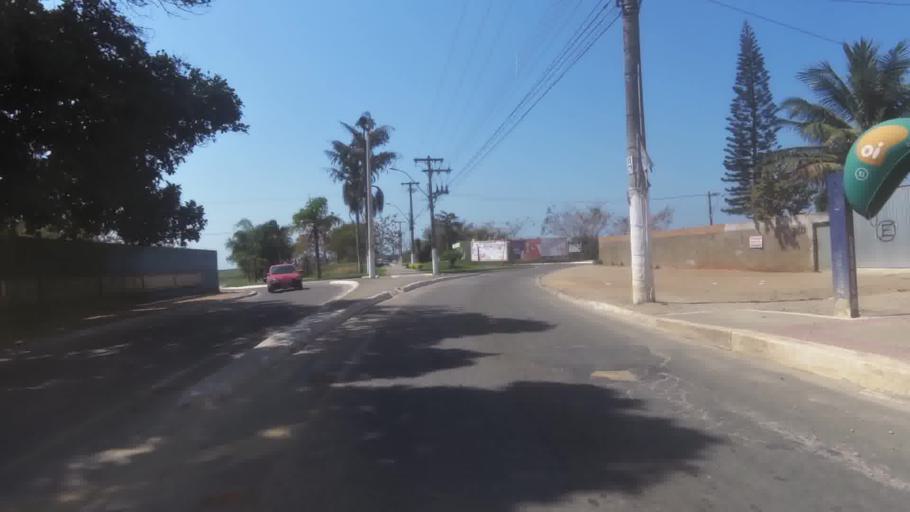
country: BR
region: Espirito Santo
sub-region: Itapemirim
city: Itapemirim
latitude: -21.0095
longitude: -40.8278
